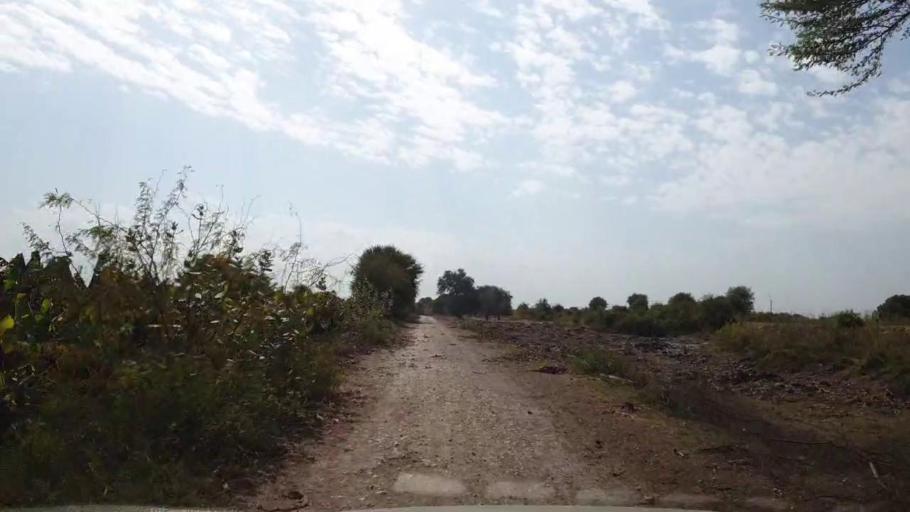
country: PK
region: Sindh
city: Matiari
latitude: 25.5464
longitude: 68.5470
